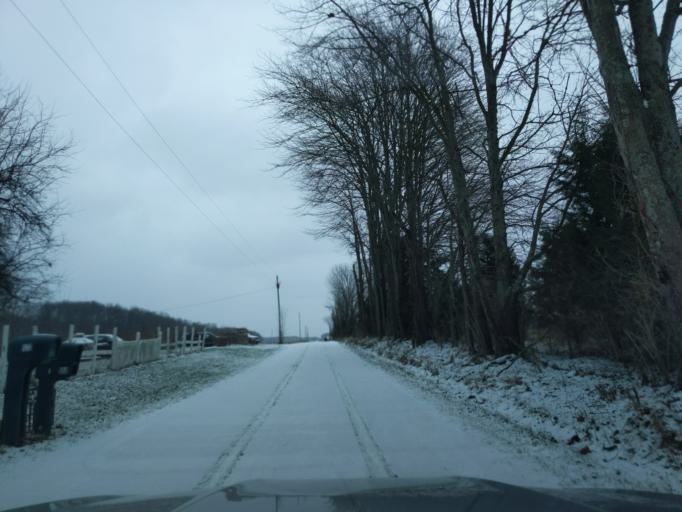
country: US
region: Indiana
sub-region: Decatur County
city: Westport
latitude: 39.2048
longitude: -85.4827
